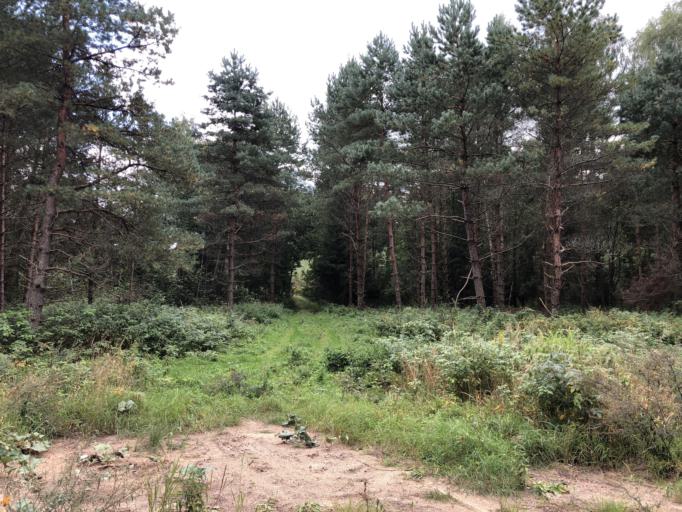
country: LV
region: Vecumnieki
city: Vecumnieki
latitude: 56.6483
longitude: 24.4707
